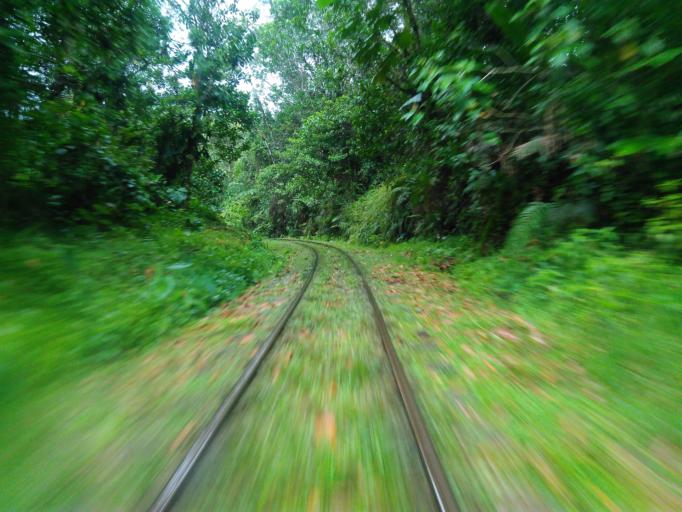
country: CO
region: Valle del Cauca
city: Buenaventura
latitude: 3.8435
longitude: -76.8905
